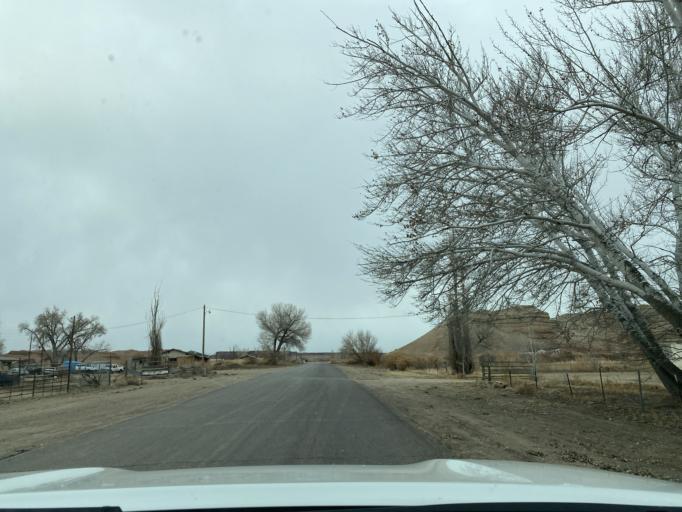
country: US
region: Utah
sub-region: Emery County
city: Ferron
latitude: 38.3720
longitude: -110.7167
